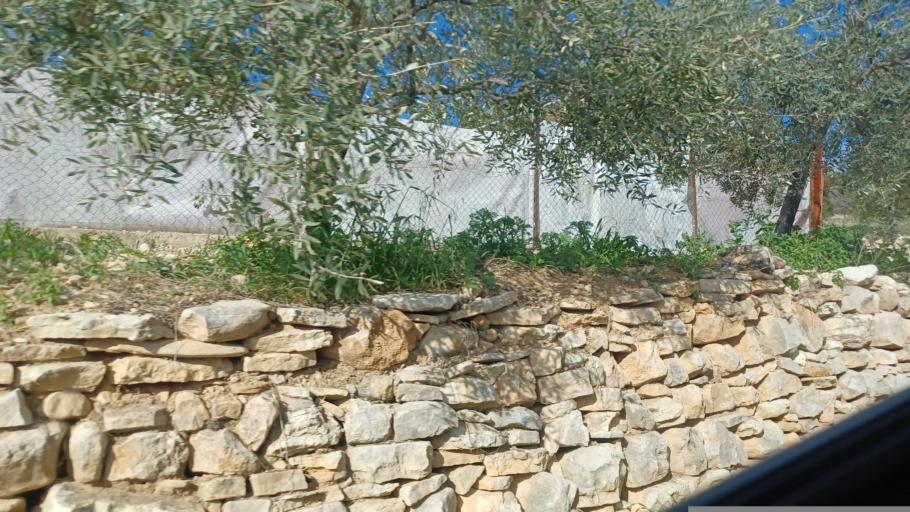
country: CY
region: Limassol
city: Pano Polemidia
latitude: 34.7857
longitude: 32.9819
